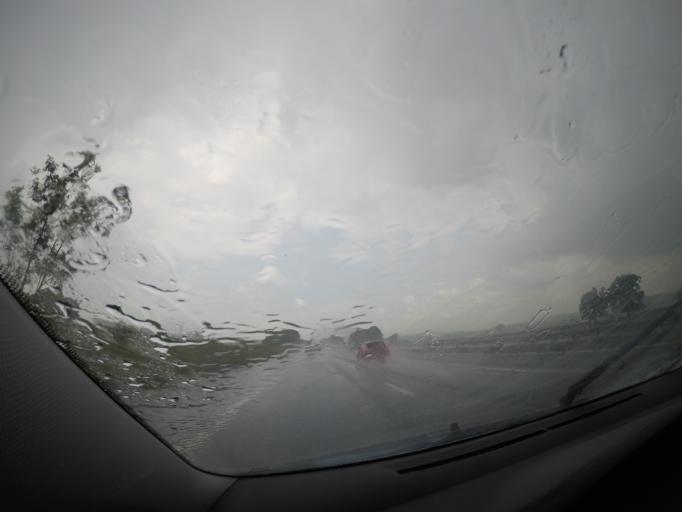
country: GB
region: England
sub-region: Cumbria
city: Penrith
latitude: 54.7122
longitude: -2.7952
